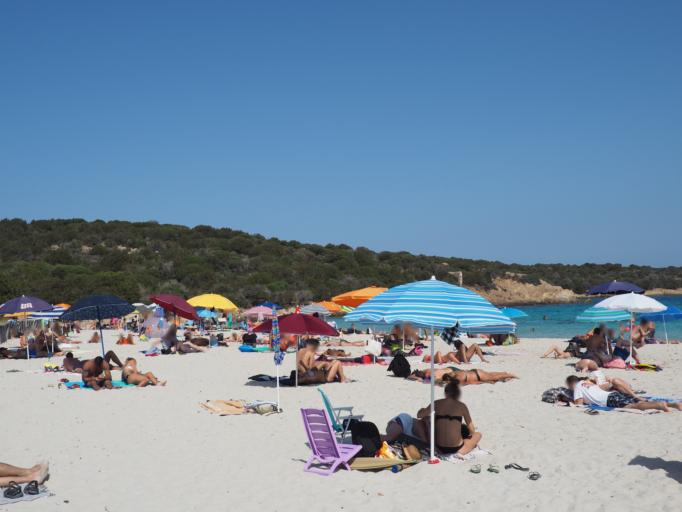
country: IT
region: Sardinia
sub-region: Provincia di Olbia-Tempio
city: Porto Cervo
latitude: 41.1810
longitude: 9.4753
